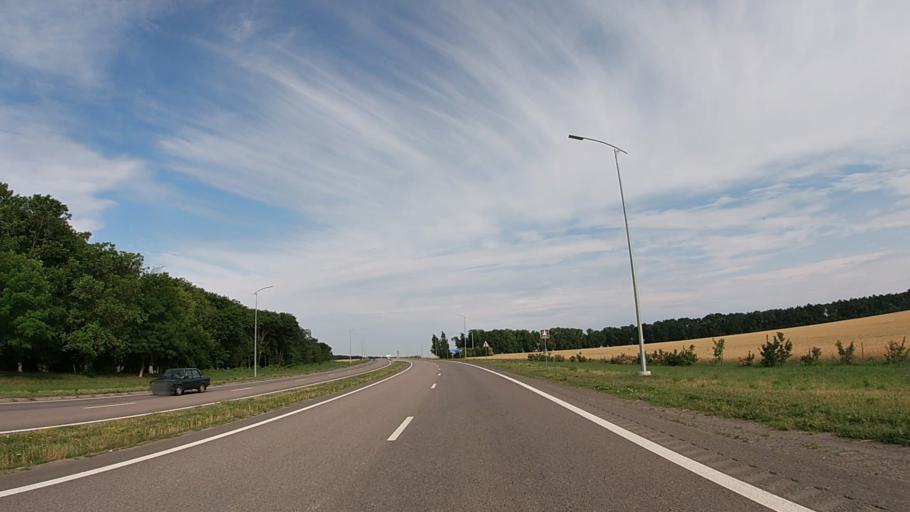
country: RU
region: Belgorod
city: Rakitnoye
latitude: 50.7619
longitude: 35.9610
